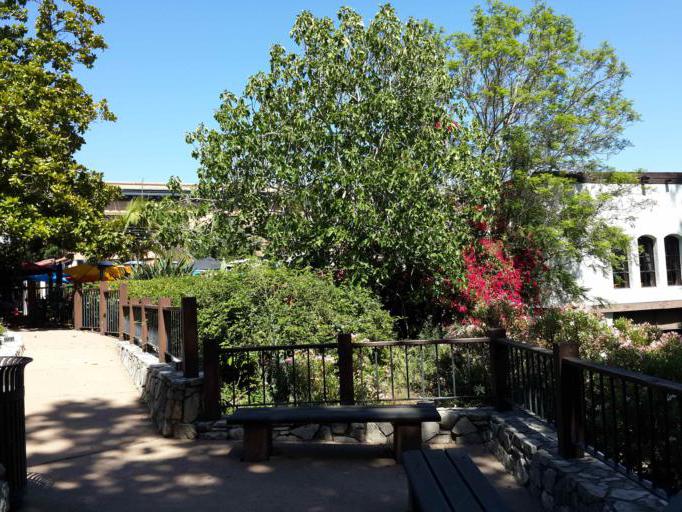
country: US
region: California
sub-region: San Luis Obispo County
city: San Luis Obispo
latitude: 35.2803
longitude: -120.6638
